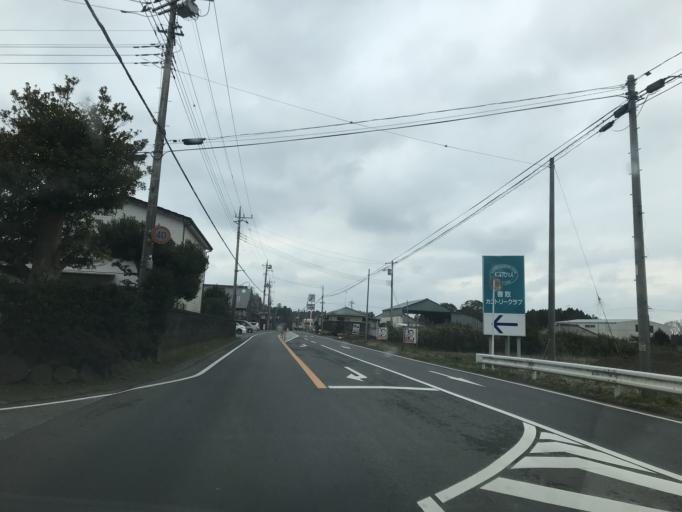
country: JP
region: Chiba
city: Sawara
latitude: 35.8615
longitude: 140.5494
